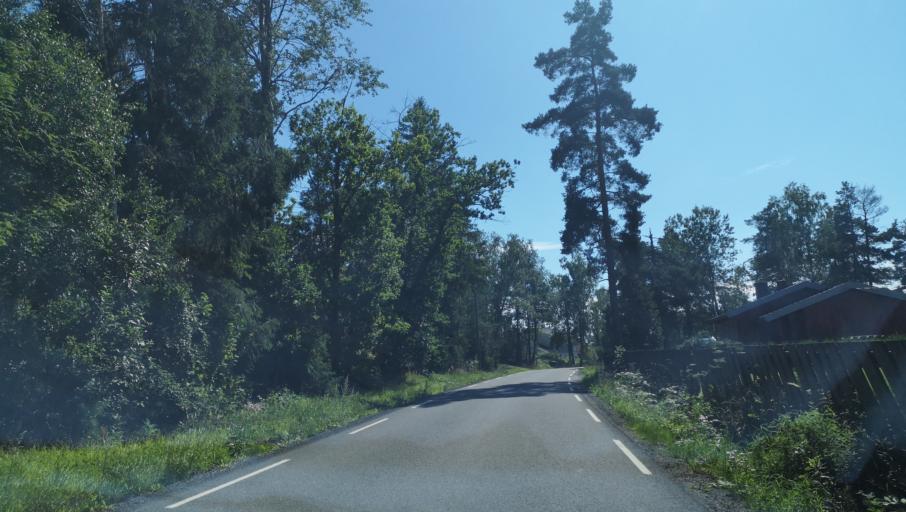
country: NO
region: Akershus
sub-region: Vestby
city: Vestby
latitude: 59.5381
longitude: 10.6905
